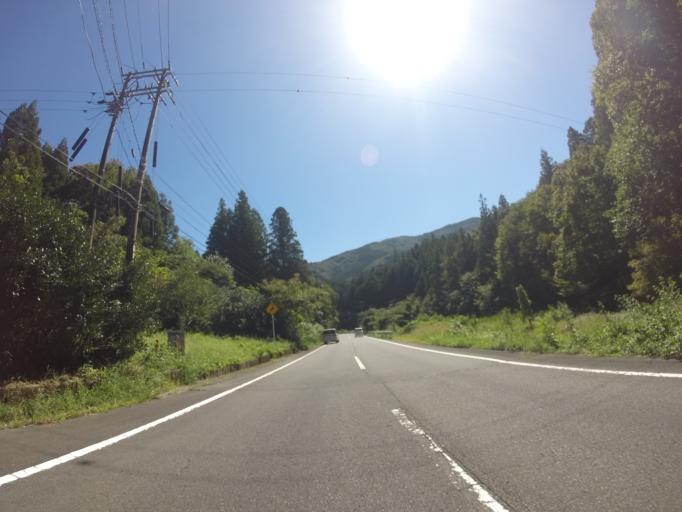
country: JP
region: Shizuoka
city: Kanaya
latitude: 34.9050
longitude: 138.1170
